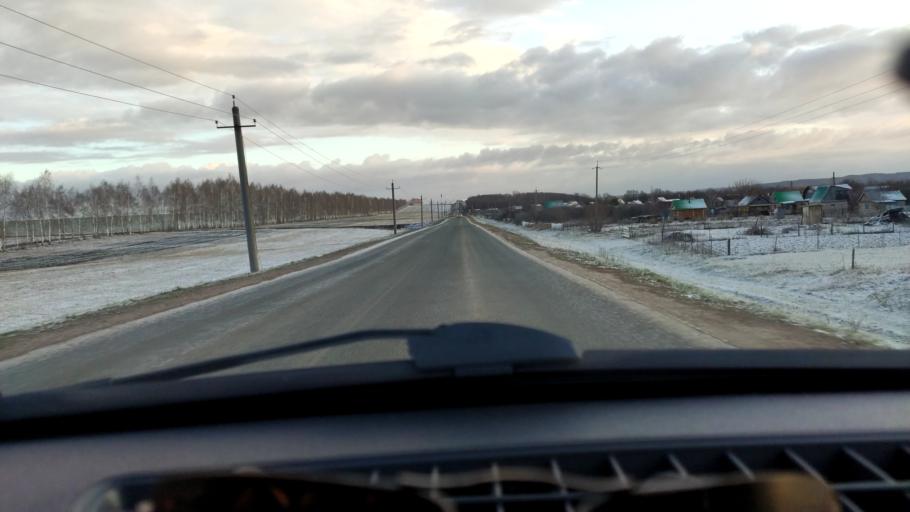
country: RU
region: Bashkortostan
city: Kabakovo
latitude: 54.5133
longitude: 56.1615
